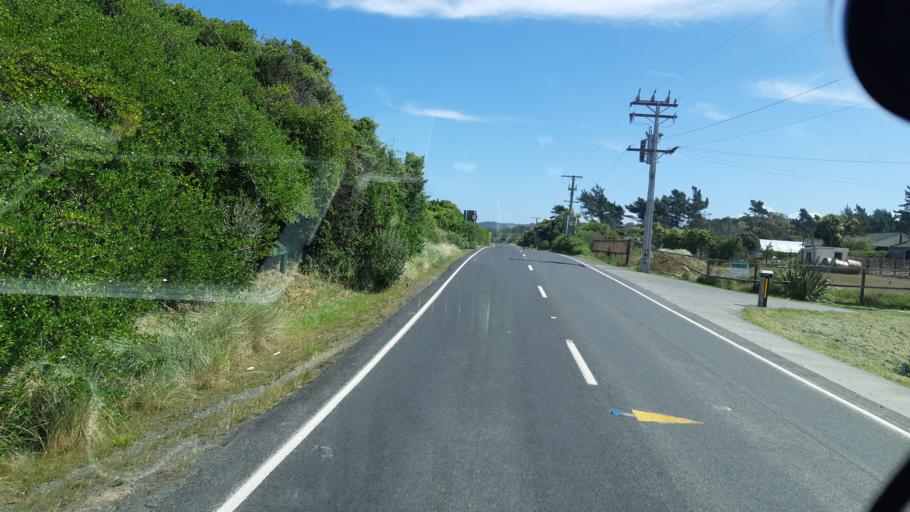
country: NZ
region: Otago
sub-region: Dunedin City
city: Dunedin
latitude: -45.9514
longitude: 170.3228
